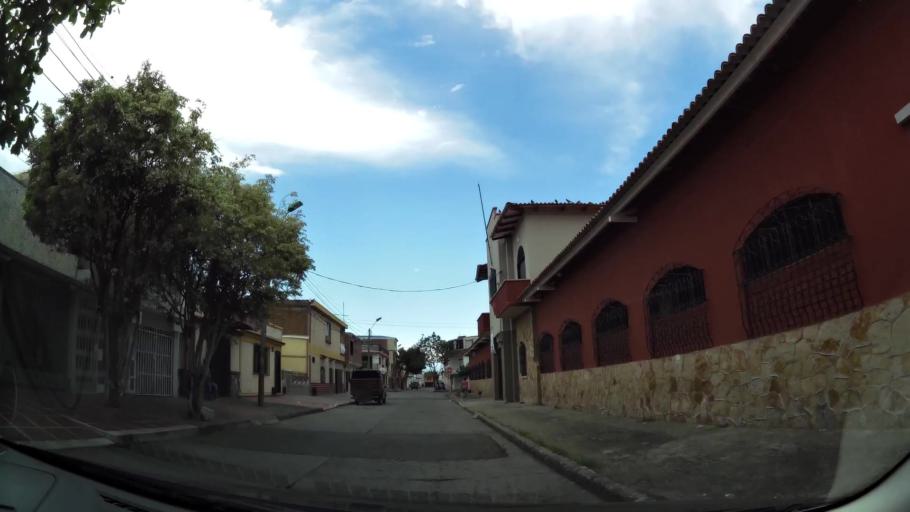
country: CO
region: Valle del Cauca
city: Cali
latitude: 3.4398
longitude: -76.5220
